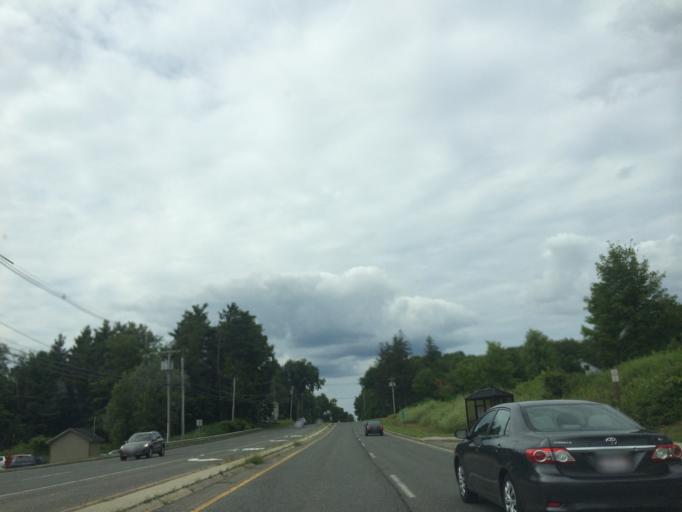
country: US
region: Massachusetts
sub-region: Berkshire County
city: Lenox
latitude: 42.3776
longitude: -73.2769
